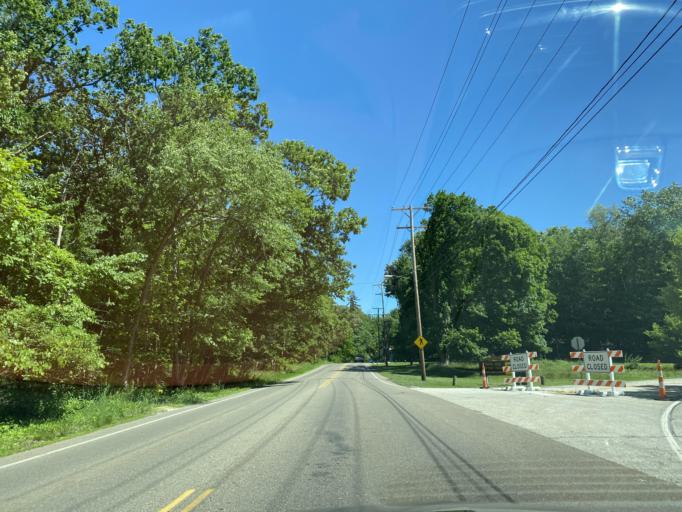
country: US
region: Ohio
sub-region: Summit County
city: Akron
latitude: 41.1317
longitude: -81.5438
